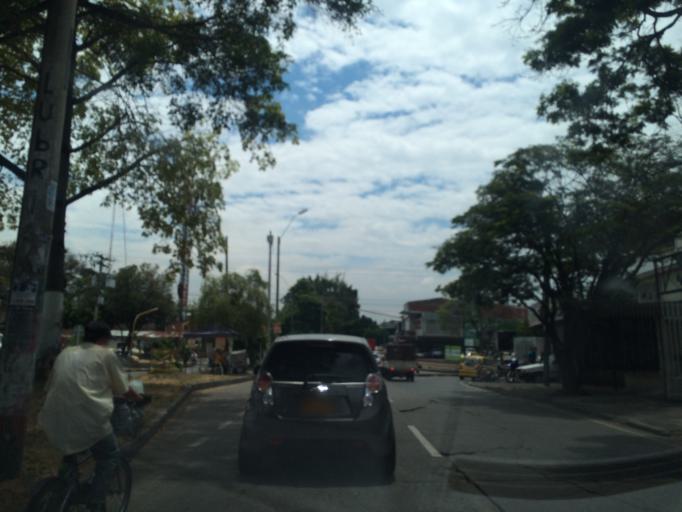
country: CO
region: Valle del Cauca
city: Cali
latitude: 3.4115
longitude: -76.5254
